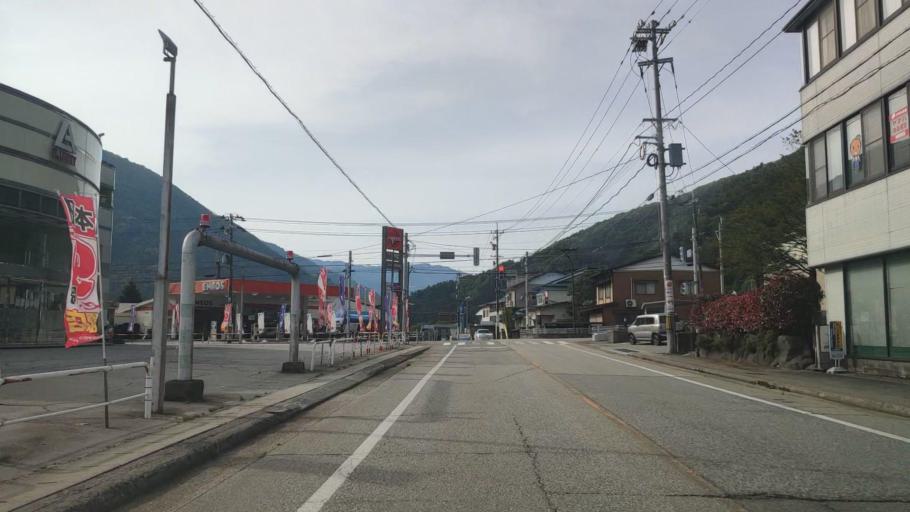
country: JP
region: Gifu
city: Takayama
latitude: 36.3269
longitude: 137.3079
